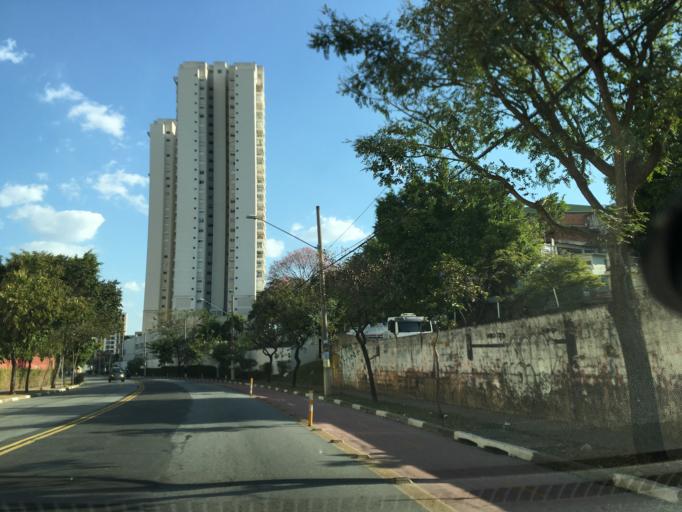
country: BR
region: Sao Paulo
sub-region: Sao Paulo
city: Sao Paulo
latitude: -23.4792
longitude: -46.6451
